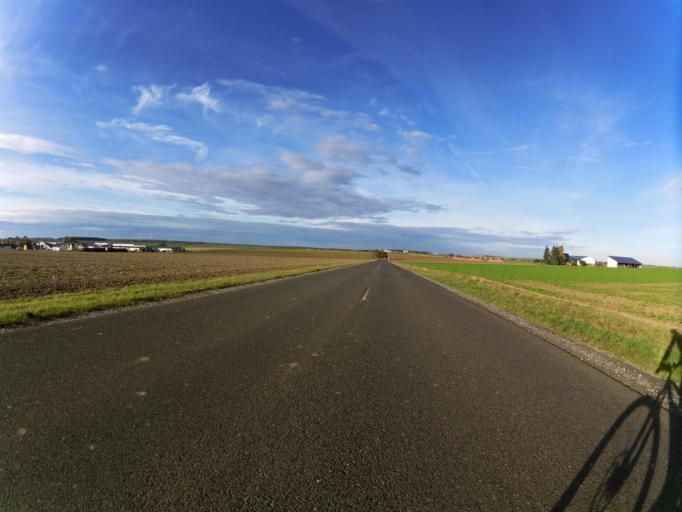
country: DE
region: Bavaria
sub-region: Regierungsbezirk Unterfranken
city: Giebelstadt
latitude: 49.6557
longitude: 9.9522
